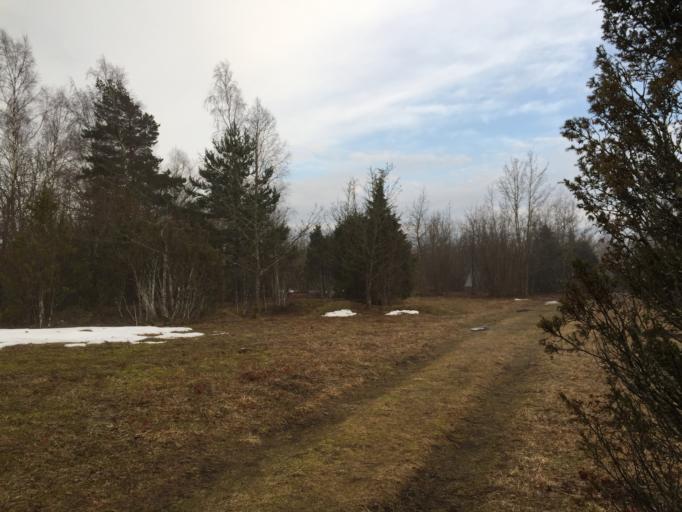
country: EE
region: Laeaene
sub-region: Ridala Parish
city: Uuemoisa
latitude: 58.6910
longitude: 23.5812
